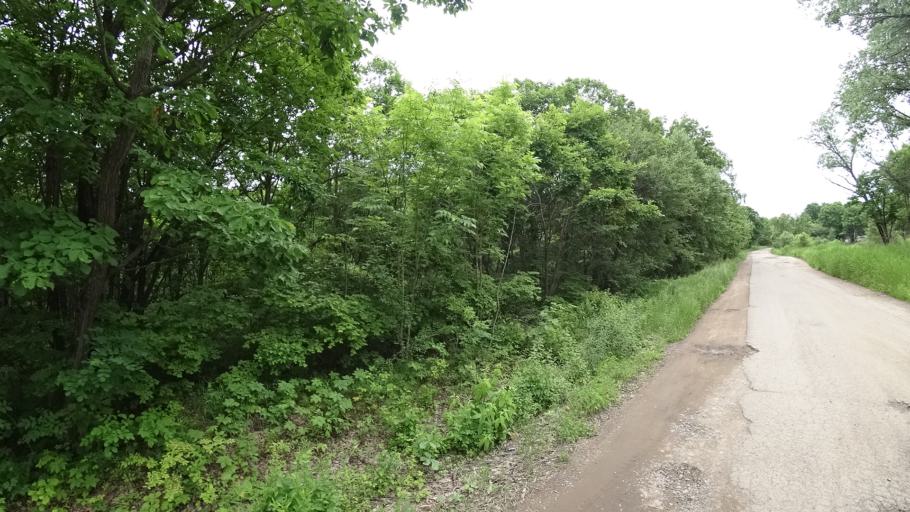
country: RU
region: Primorskiy
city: Novosysoyevka
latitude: 44.2017
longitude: 133.3200
